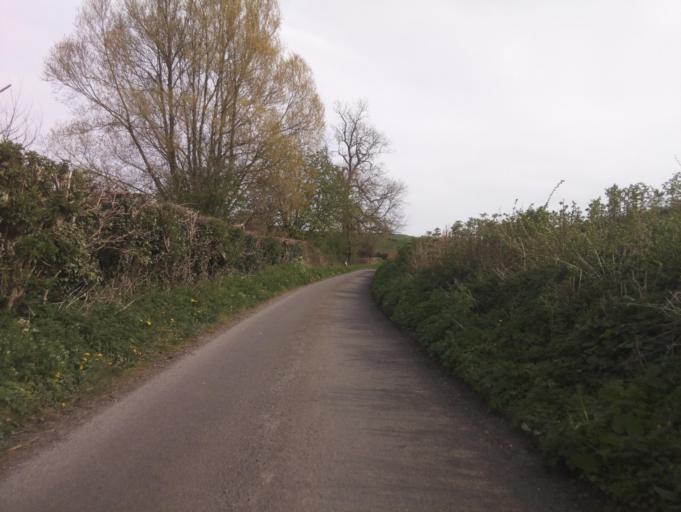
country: GB
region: England
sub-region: Somerset
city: Milborne Port
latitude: 50.9771
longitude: -2.4963
